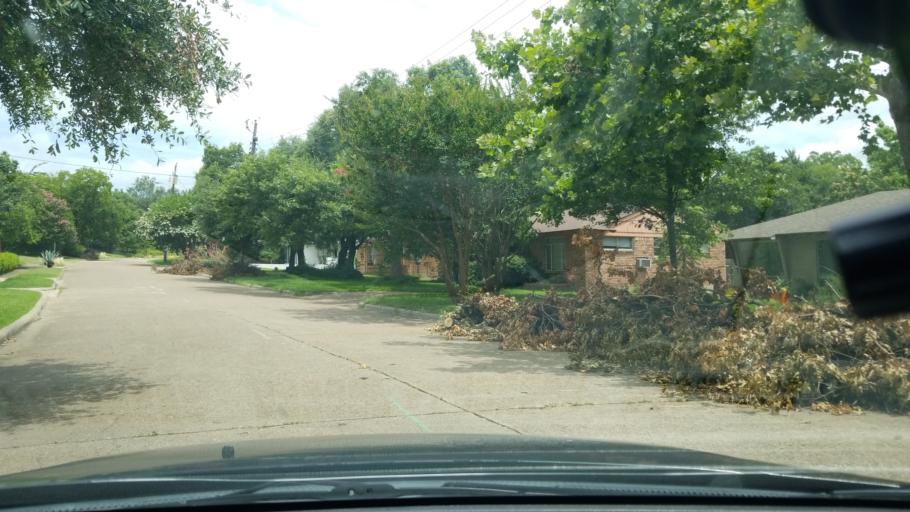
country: US
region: Texas
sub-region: Dallas County
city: Garland
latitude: 32.8251
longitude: -96.6877
